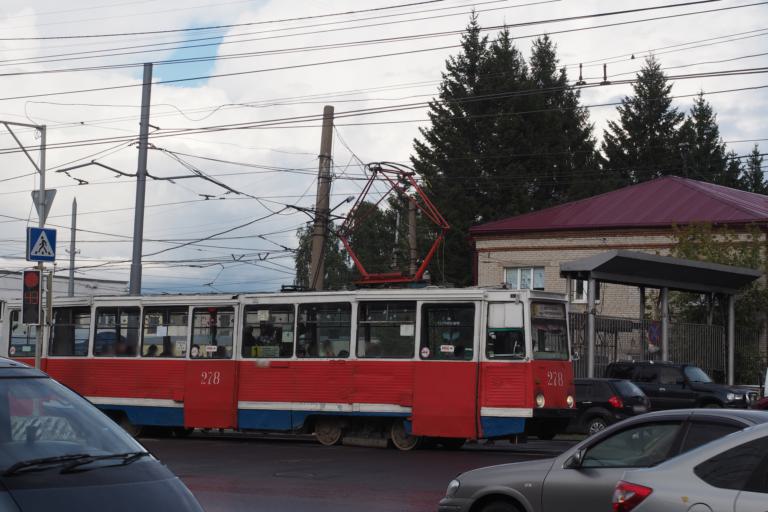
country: RU
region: Tomsk
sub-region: Tomskiy Rayon
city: Tomsk
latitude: 56.4688
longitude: 84.9814
